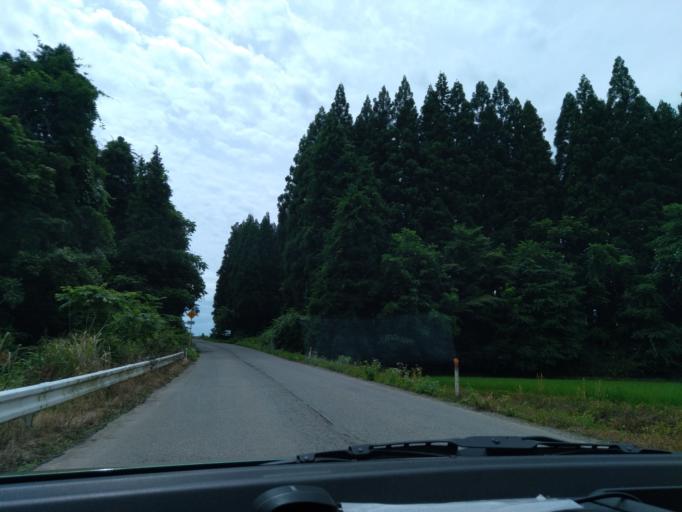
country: JP
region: Akita
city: Kakunodatemachi
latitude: 39.5890
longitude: 140.6193
